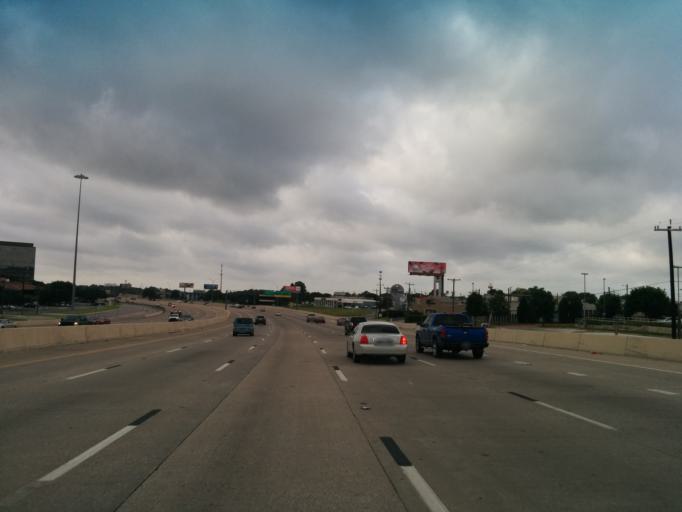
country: US
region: Texas
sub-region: Bexar County
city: Balcones Heights
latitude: 29.4912
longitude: -98.5466
